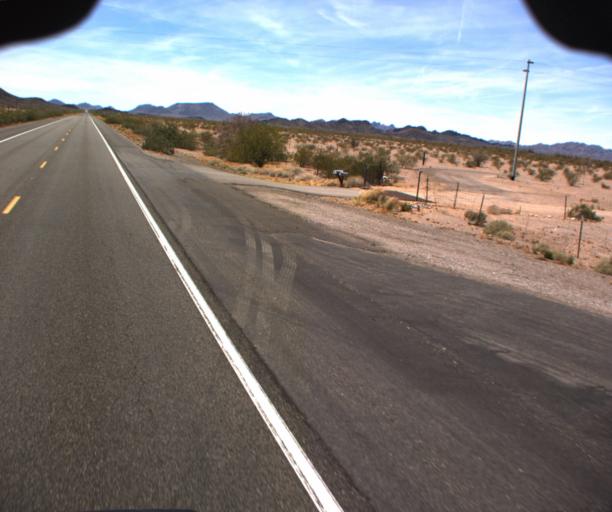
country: US
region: Arizona
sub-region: La Paz County
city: Salome
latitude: 33.6915
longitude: -113.8960
